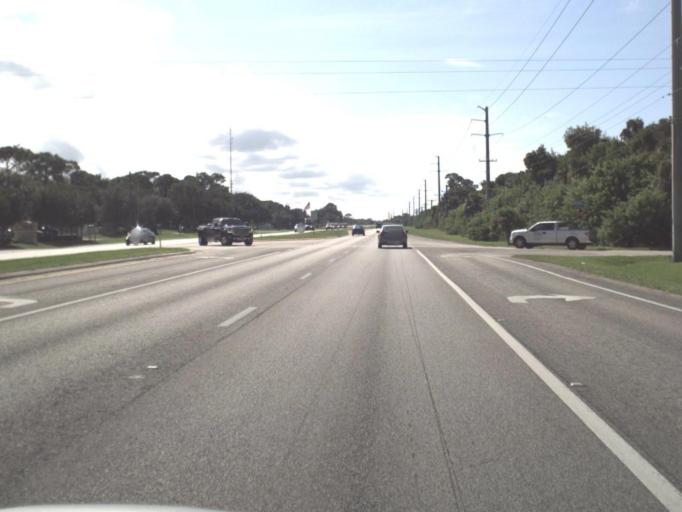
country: US
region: Florida
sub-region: Sarasota County
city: Laurel
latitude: 27.1609
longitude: -82.4730
